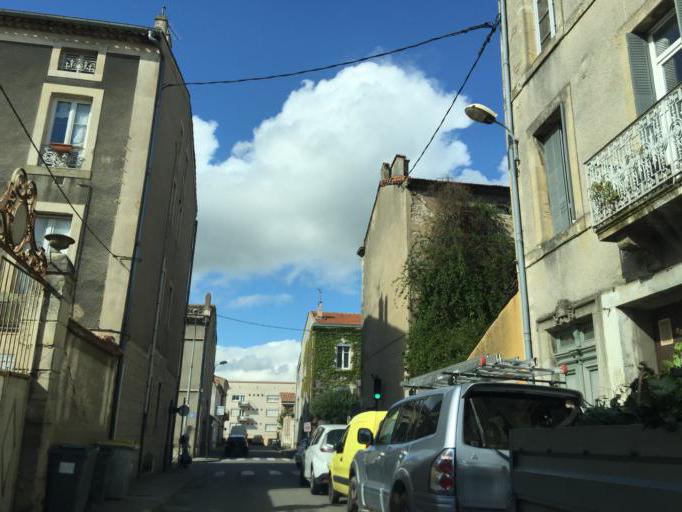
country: FR
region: Languedoc-Roussillon
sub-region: Departement de l'Aude
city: Carcassonne
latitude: 43.2159
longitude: 2.3571
